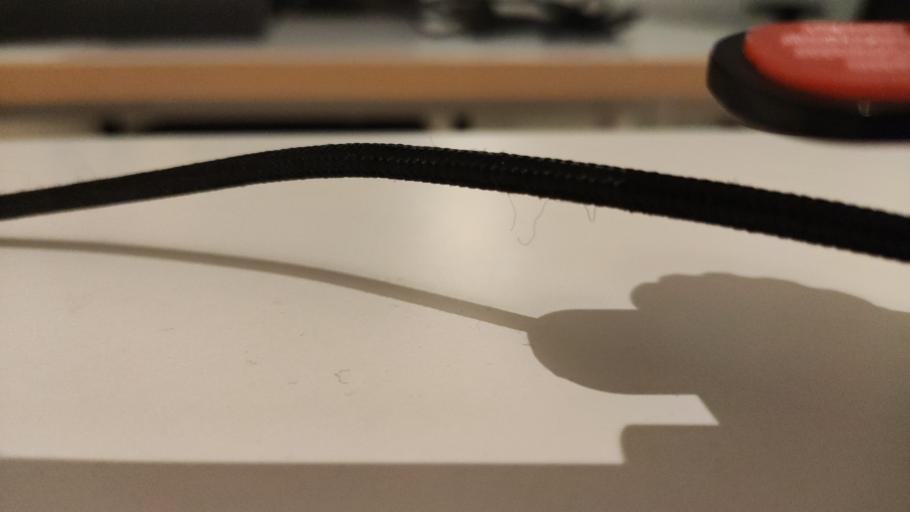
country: RU
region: Moskovskaya
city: Kurovskoye
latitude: 55.5348
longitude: 38.8727
